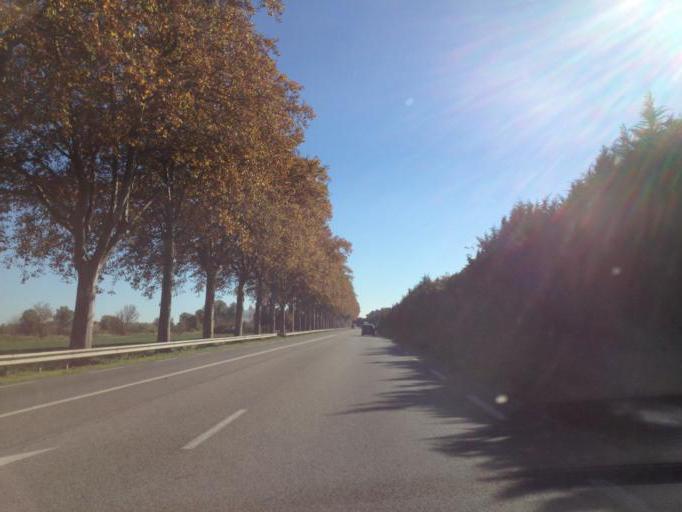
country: FR
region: Provence-Alpes-Cote d'Azur
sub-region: Departement du Vaucluse
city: Courthezon
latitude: 44.0722
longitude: 4.8834
